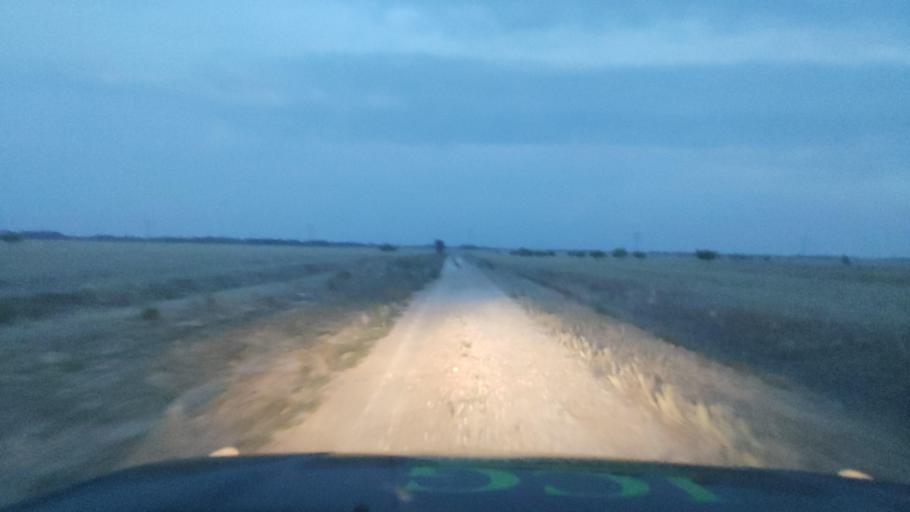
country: KZ
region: Pavlodar
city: Koktobe
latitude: 51.9694
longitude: 77.5921
